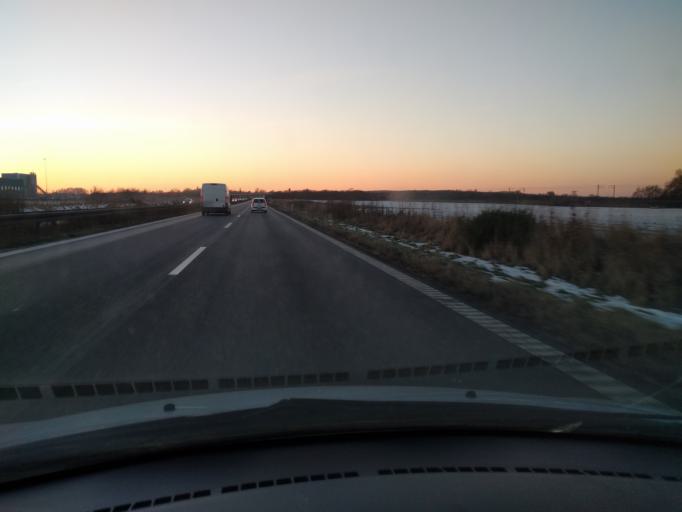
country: DK
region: Zealand
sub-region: Slagelse Kommune
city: Forlev
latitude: 55.3636
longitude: 11.2357
